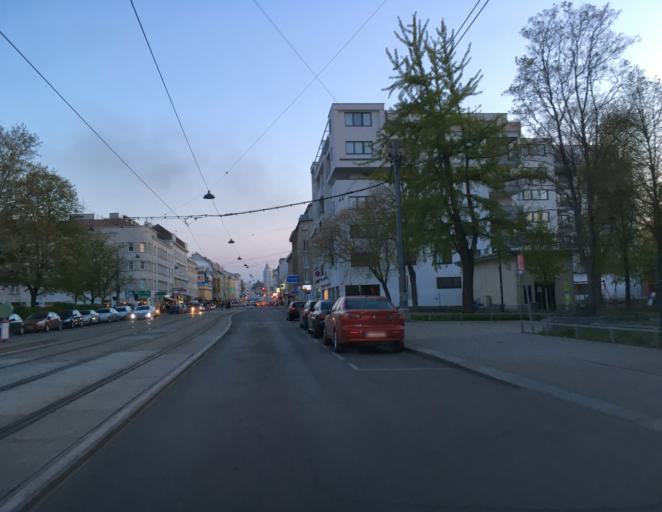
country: AT
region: Vienna
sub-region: Wien Stadt
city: Vienna
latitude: 48.2616
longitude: 16.3999
